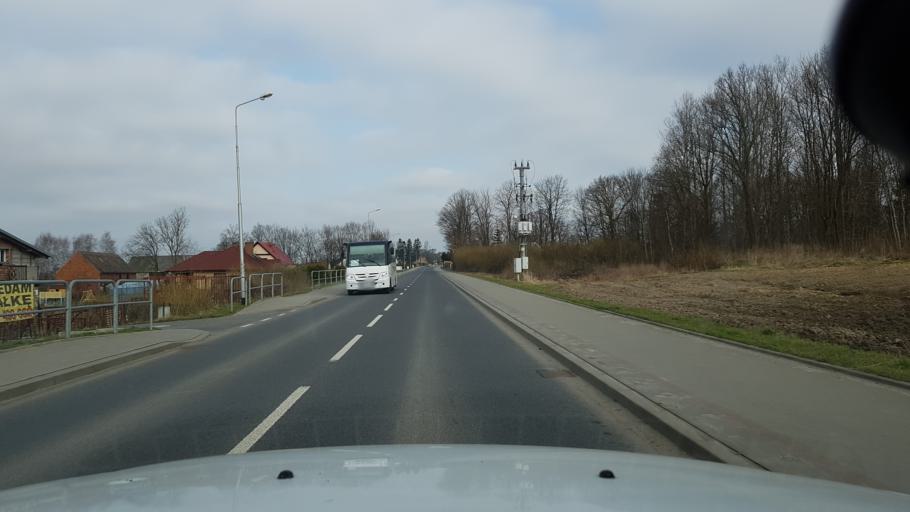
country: PL
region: West Pomeranian Voivodeship
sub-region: Powiat koszalinski
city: Sianow
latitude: 54.2511
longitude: 16.2792
